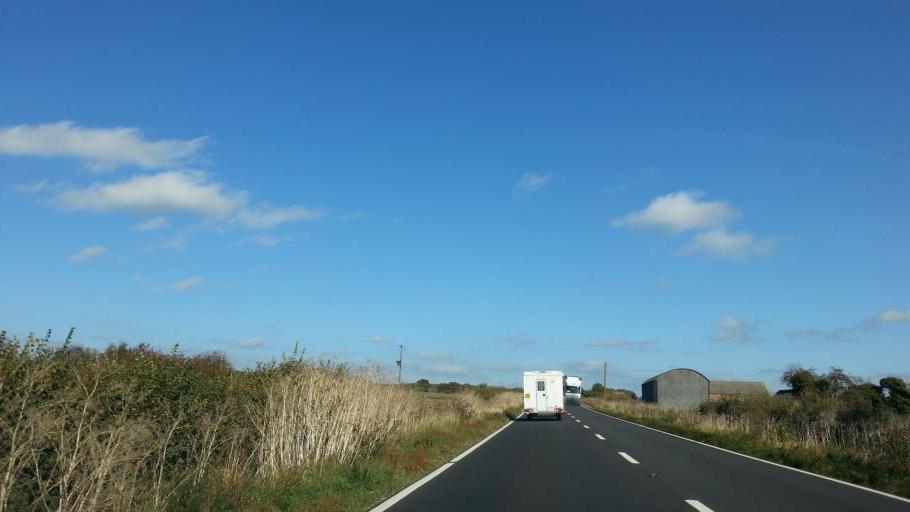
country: GB
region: England
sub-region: Northamptonshire
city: Oundle
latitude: 52.4272
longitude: -0.4886
